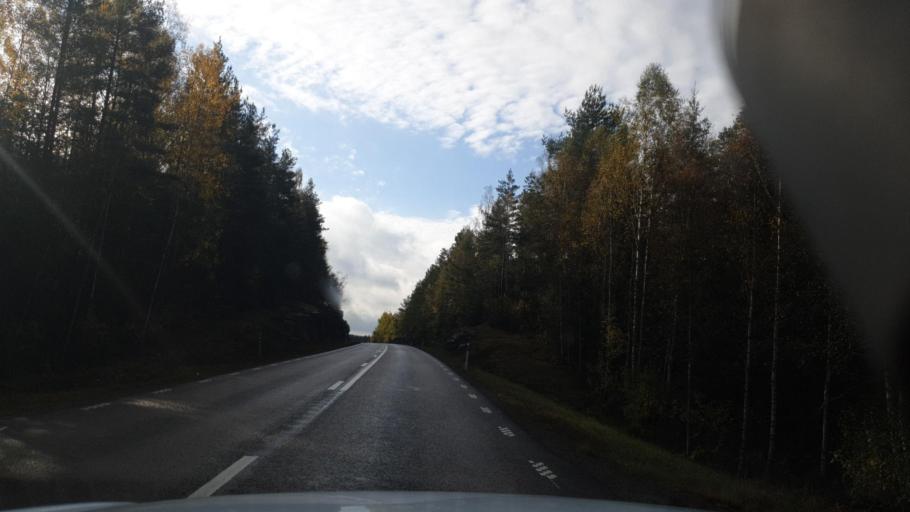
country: SE
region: Vaermland
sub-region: Arvika Kommun
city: Arvika
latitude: 59.4917
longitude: 12.7607
